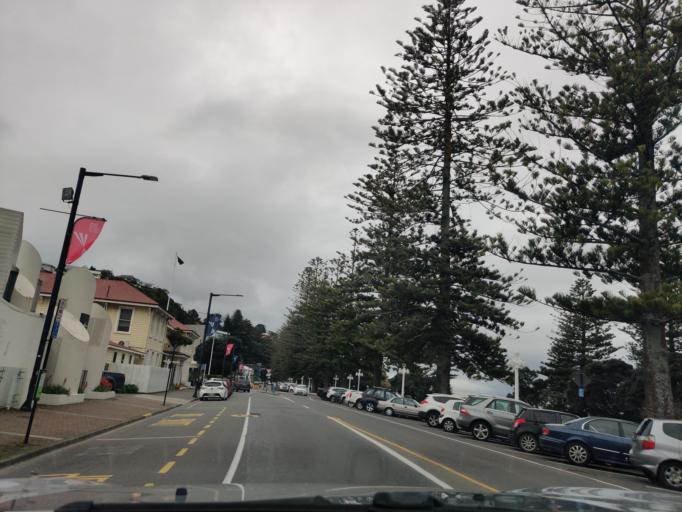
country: NZ
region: Hawke's Bay
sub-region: Napier City
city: Napier
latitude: -39.4890
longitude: 176.9193
